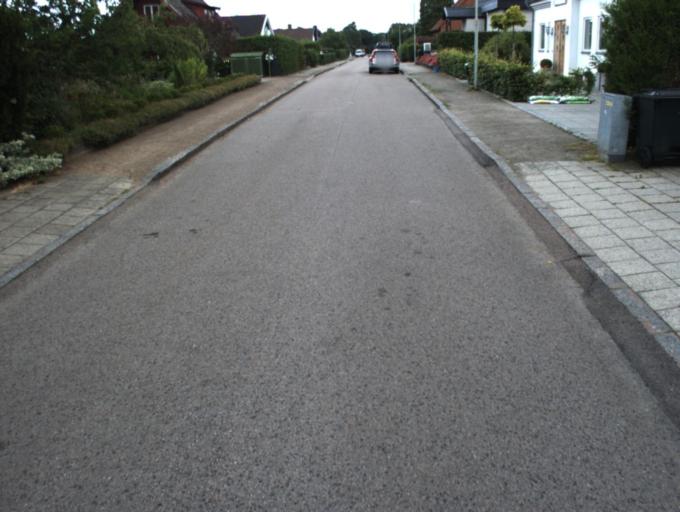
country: SE
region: Skane
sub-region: Helsingborg
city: Helsingborg
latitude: 56.0455
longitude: 12.7295
